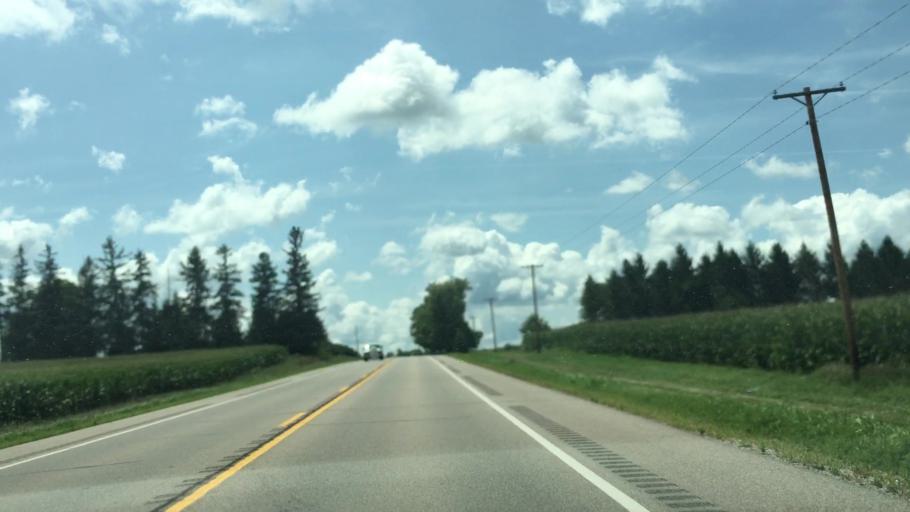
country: US
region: Iowa
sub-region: Johnson County
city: Solon
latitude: 41.8188
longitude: -91.4963
